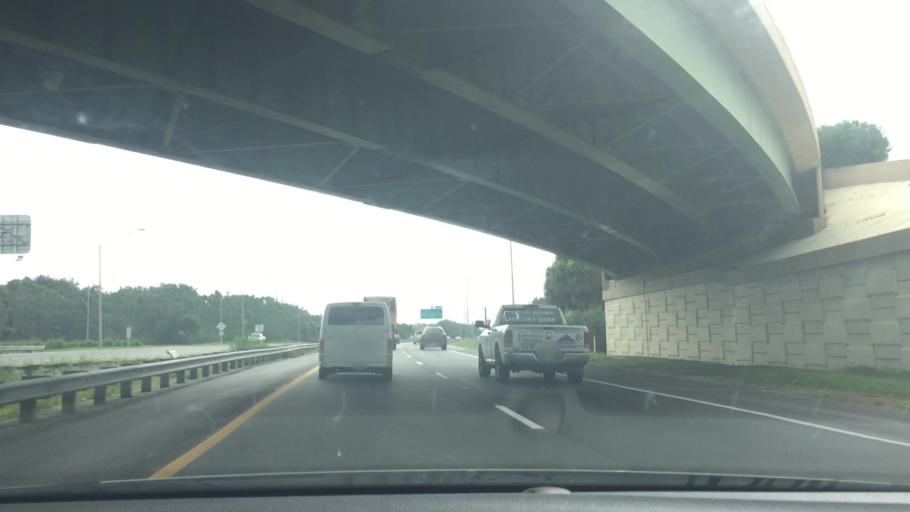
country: US
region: Florida
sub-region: Orange County
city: Gotha
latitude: 28.5448
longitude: -81.5170
